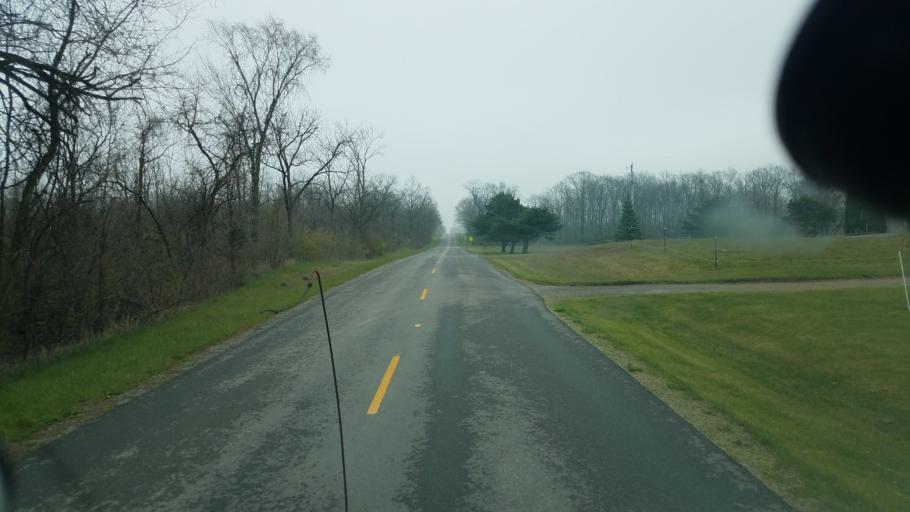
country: US
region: Ohio
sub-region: Logan County
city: Northwood
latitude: 40.4766
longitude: -83.6944
